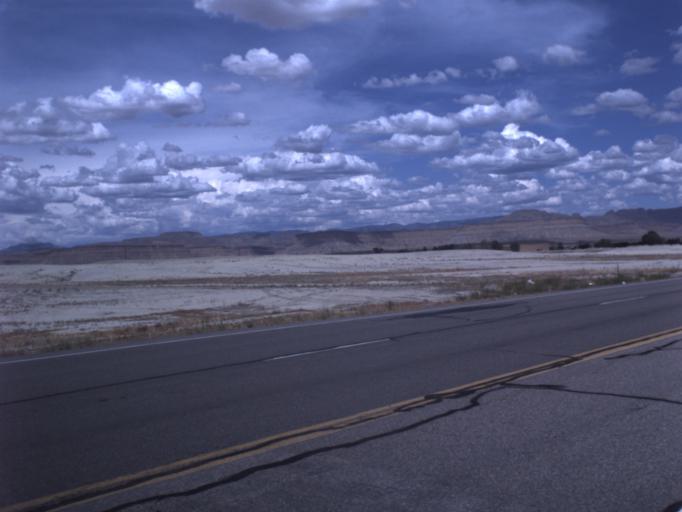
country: US
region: Utah
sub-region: Carbon County
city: East Carbon City
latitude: 38.9954
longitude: -110.1816
